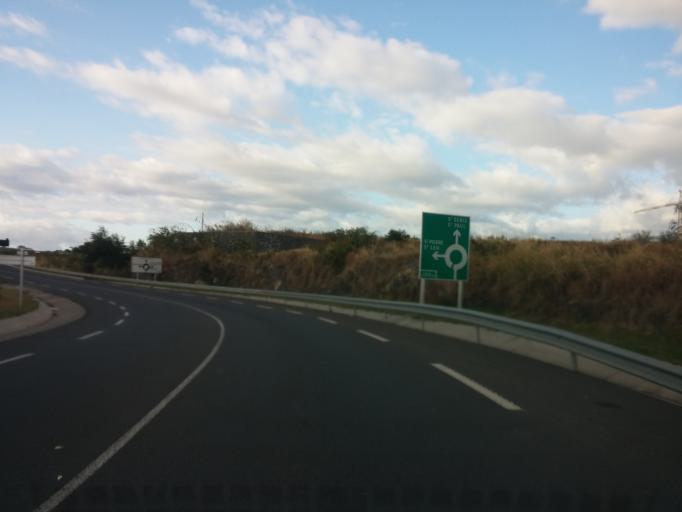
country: RE
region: Reunion
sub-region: Reunion
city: Saint-Paul
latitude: -21.0429
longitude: 55.2465
